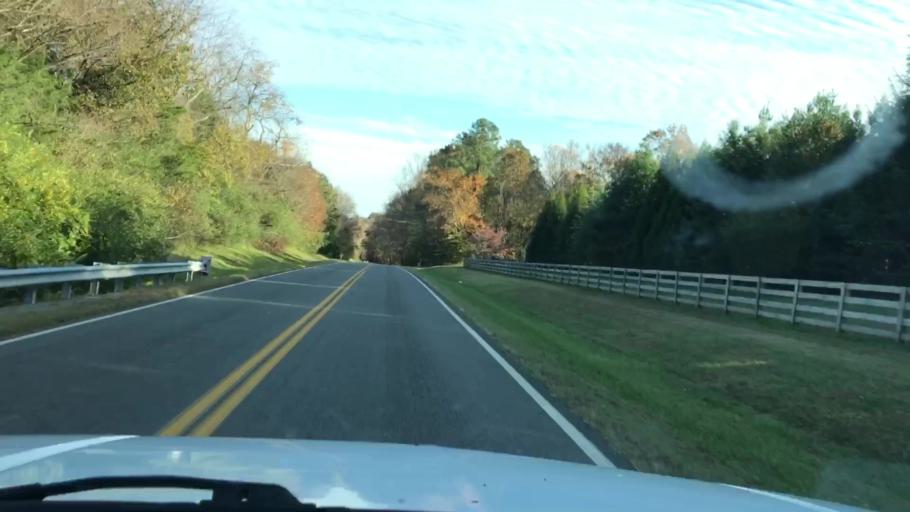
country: US
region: Virginia
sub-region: Goochland County
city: Goochland
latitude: 37.6572
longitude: -77.8572
